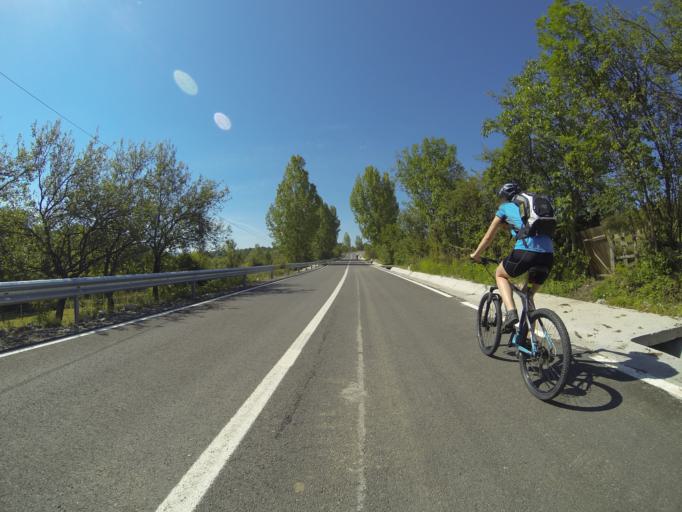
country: RO
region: Gorj
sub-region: Comuna Polovragi
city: Polovragi
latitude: 45.1747
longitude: 23.8503
